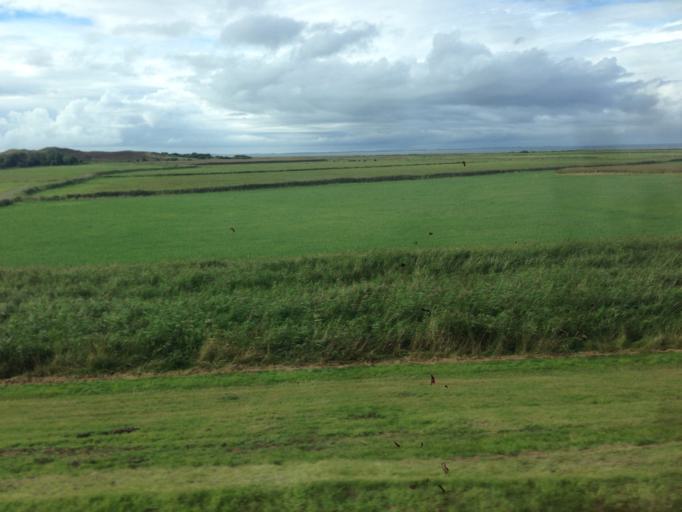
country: DE
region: Schleswig-Holstein
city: Sylt-Ost
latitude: 54.8715
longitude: 8.4755
